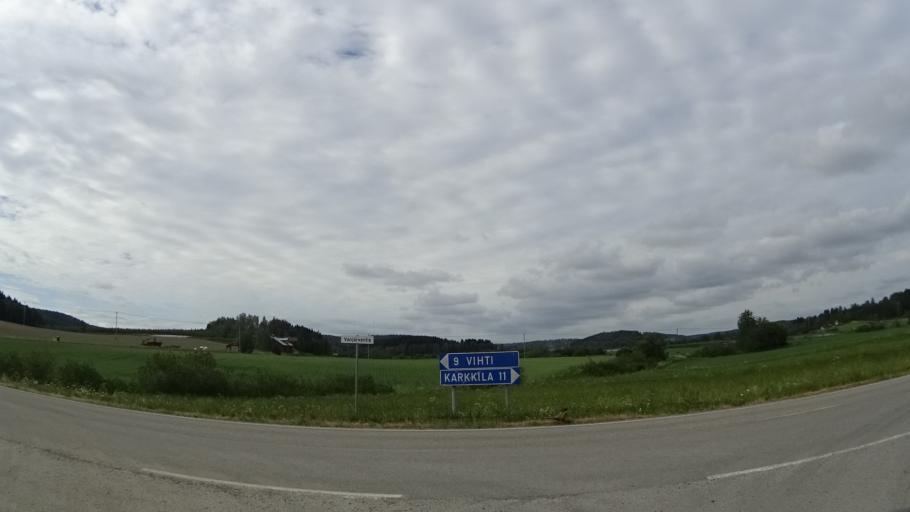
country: FI
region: Uusimaa
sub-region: Helsinki
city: Karkkila
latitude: 60.4555
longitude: 24.2386
